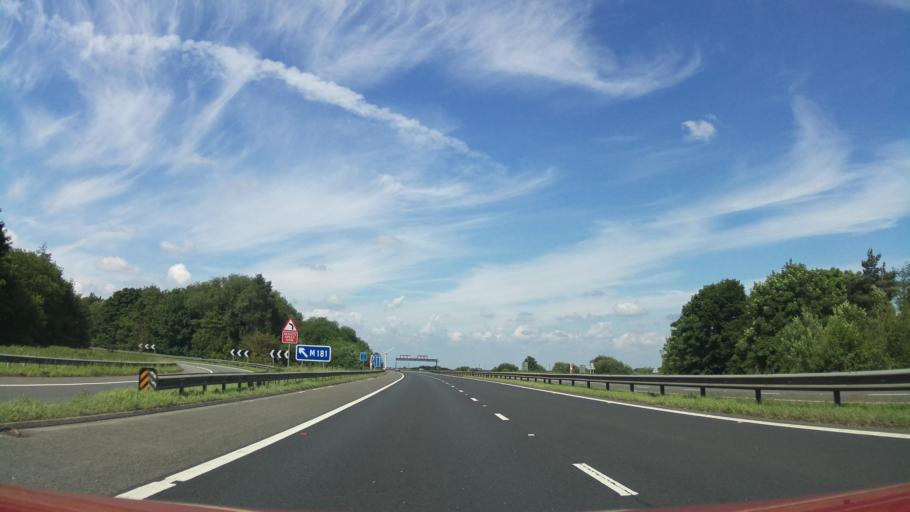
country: GB
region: England
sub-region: North Lincolnshire
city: Gunness
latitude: 53.5569
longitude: -0.7129
